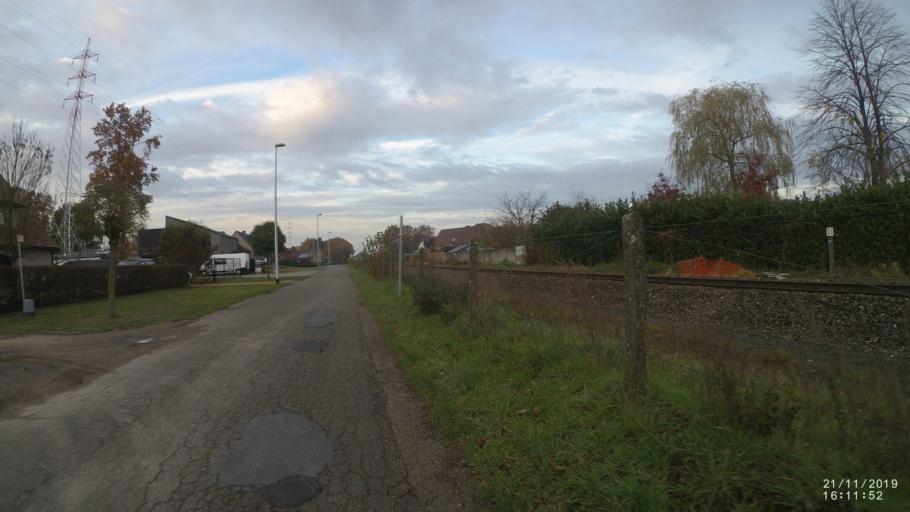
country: BE
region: Flanders
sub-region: Provincie Limburg
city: Zonhoven
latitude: 50.9932
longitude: 5.3485
